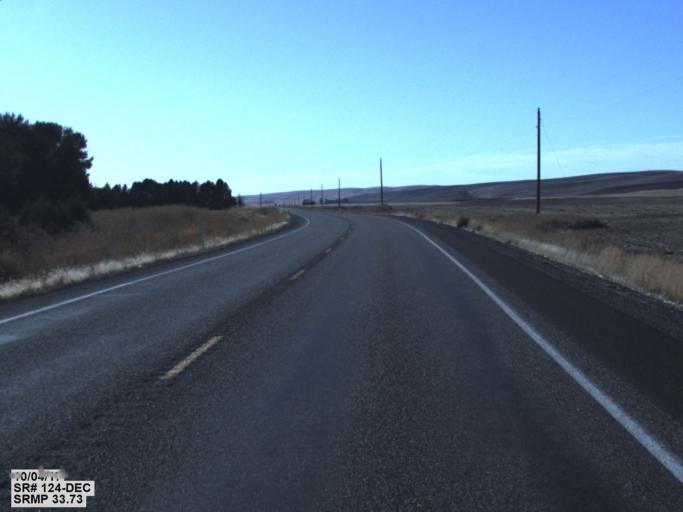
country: US
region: Washington
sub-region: Walla Walla County
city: Waitsburg
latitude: 46.3002
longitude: -118.3643
